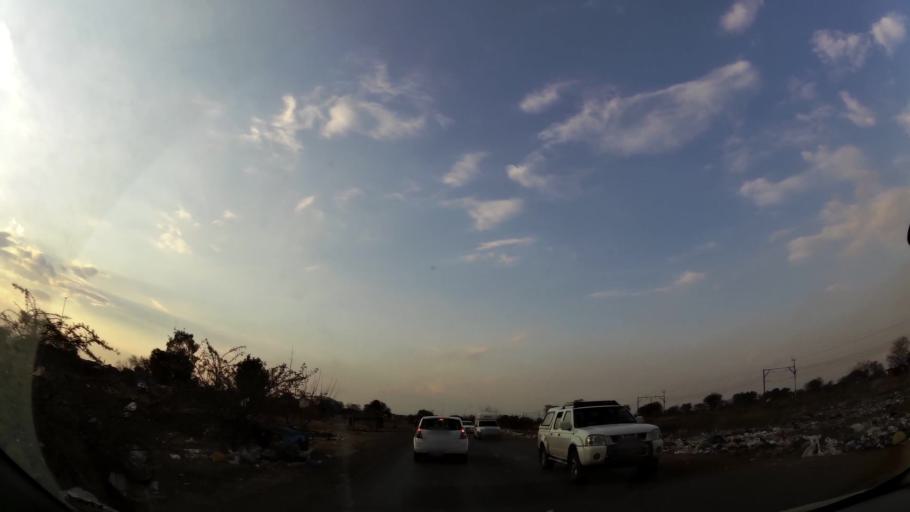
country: ZA
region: Gauteng
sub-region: City of Johannesburg Metropolitan Municipality
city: Orange Farm
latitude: -26.5758
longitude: 27.8580
